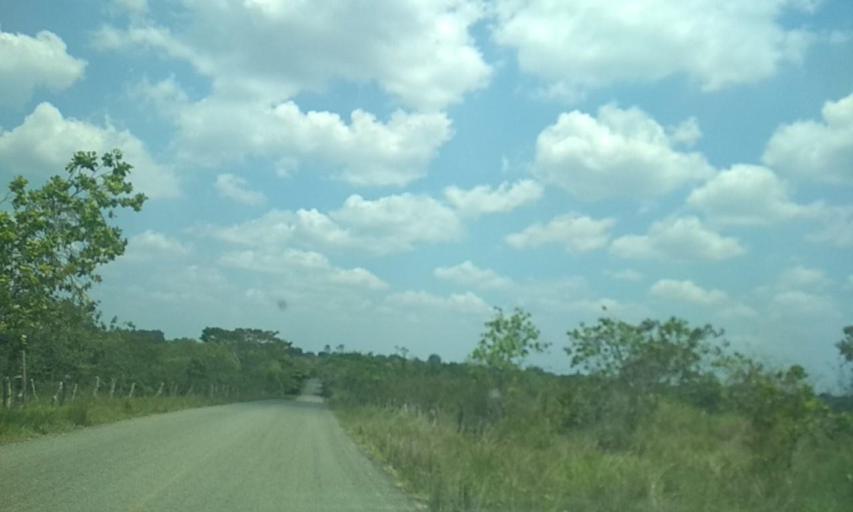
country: MX
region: Tabasco
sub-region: Huimanguillo
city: Francisco Rueda
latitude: 17.7914
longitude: -93.8405
